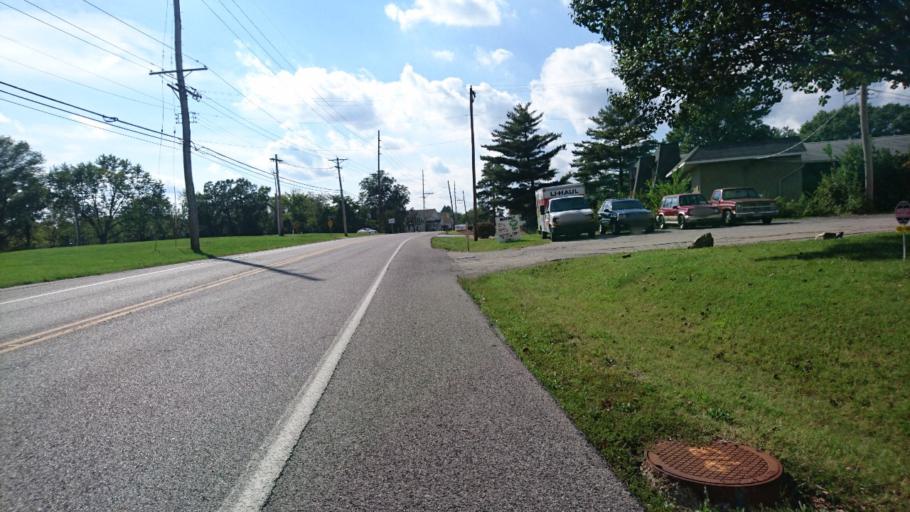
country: US
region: Missouri
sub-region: Saint Louis County
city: Wildwood
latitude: 38.5765
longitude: -90.6346
